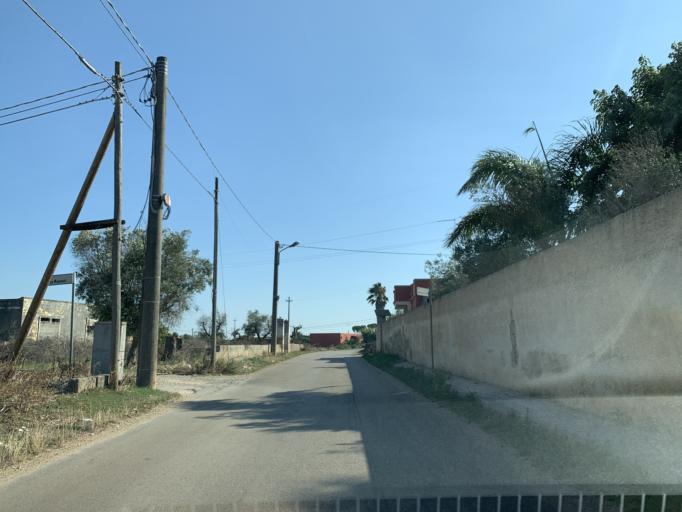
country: IT
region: Apulia
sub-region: Provincia di Lecce
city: Copertino
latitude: 40.2656
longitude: 18.0331
